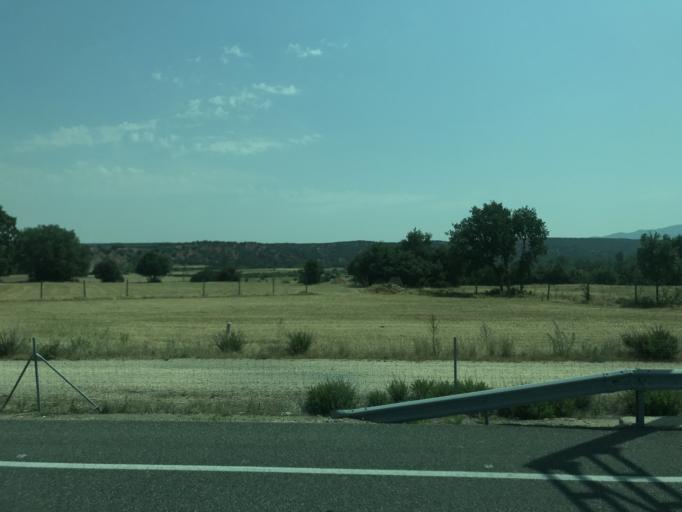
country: ES
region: Castille and Leon
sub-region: Provincia de Segovia
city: Castillejo de Mesleon
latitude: 41.2747
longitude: -3.6015
